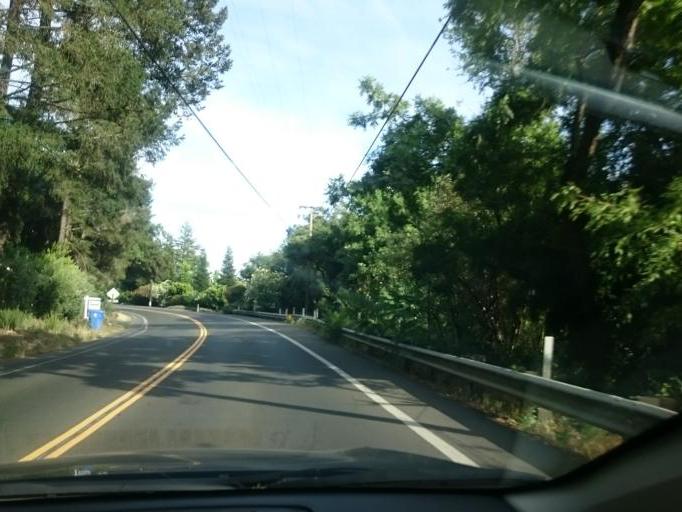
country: US
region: California
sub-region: Napa County
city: Deer Park
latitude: 38.5202
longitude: -122.4719
